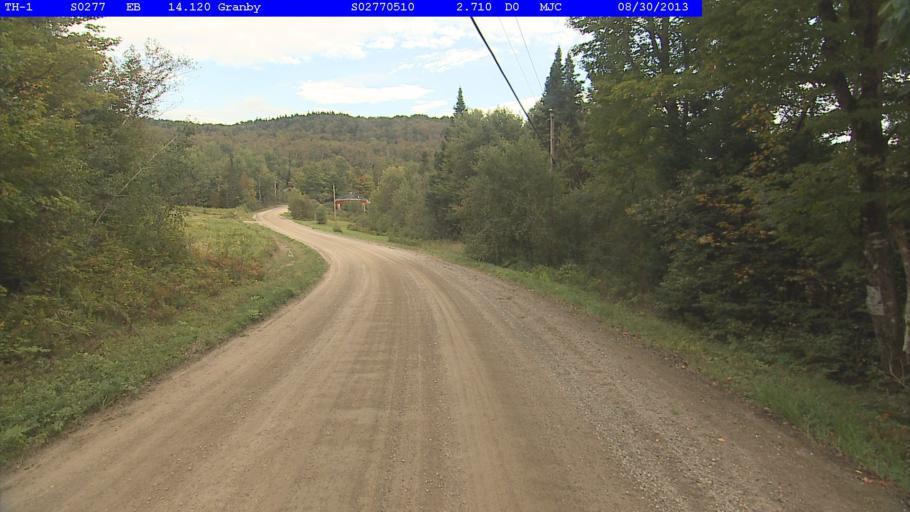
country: US
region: Vermont
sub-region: Essex County
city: Guildhall
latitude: 44.5760
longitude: -71.7134
